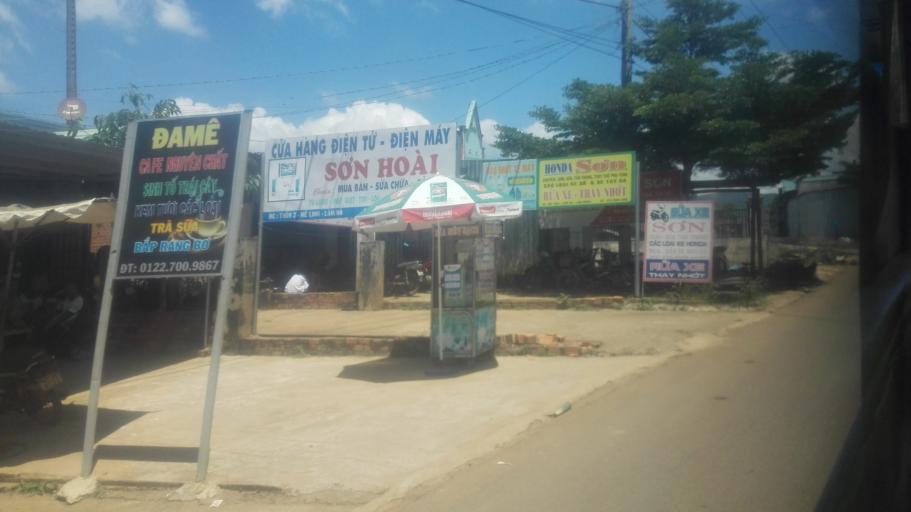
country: VN
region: Lam Dong
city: Da Lat
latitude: 11.8786
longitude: 108.3424
